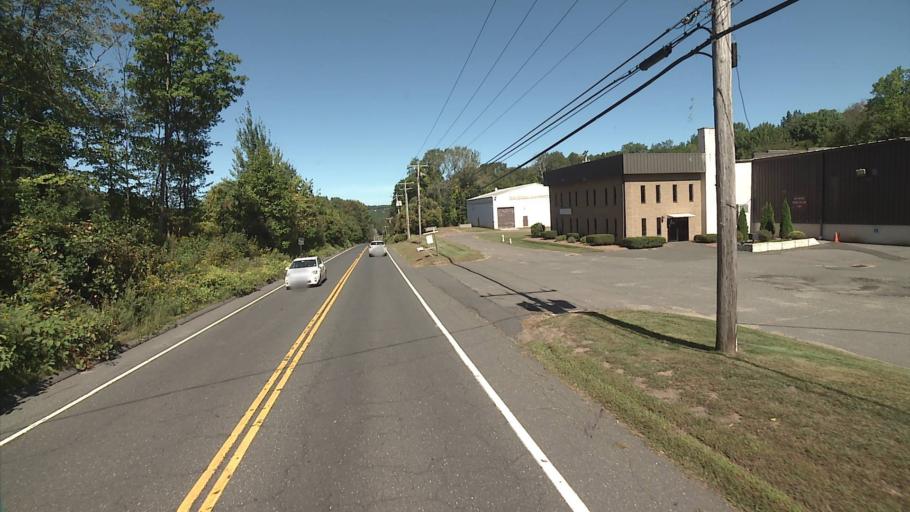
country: US
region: Connecticut
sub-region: New Haven County
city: Prospect
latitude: 41.4749
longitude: -72.9687
